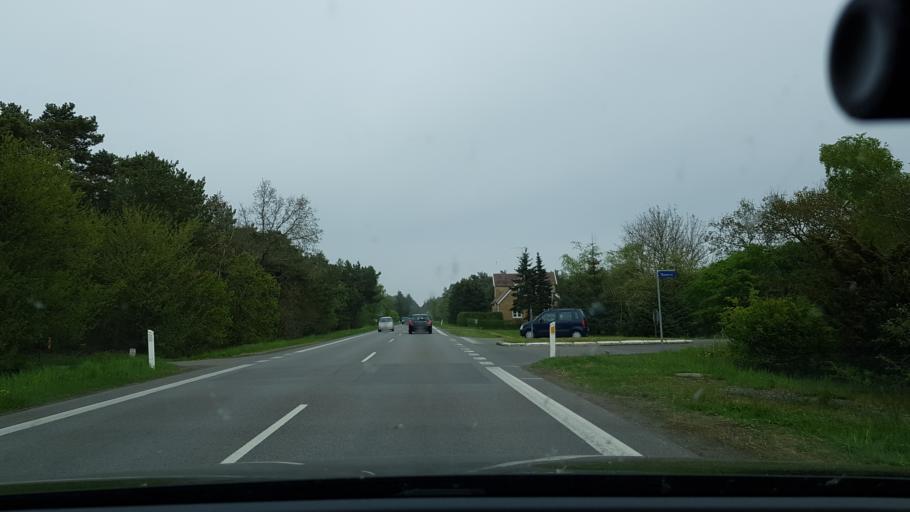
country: DK
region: Capital Region
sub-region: Bornholm Kommune
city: Nexo
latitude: 55.0453
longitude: 15.1089
